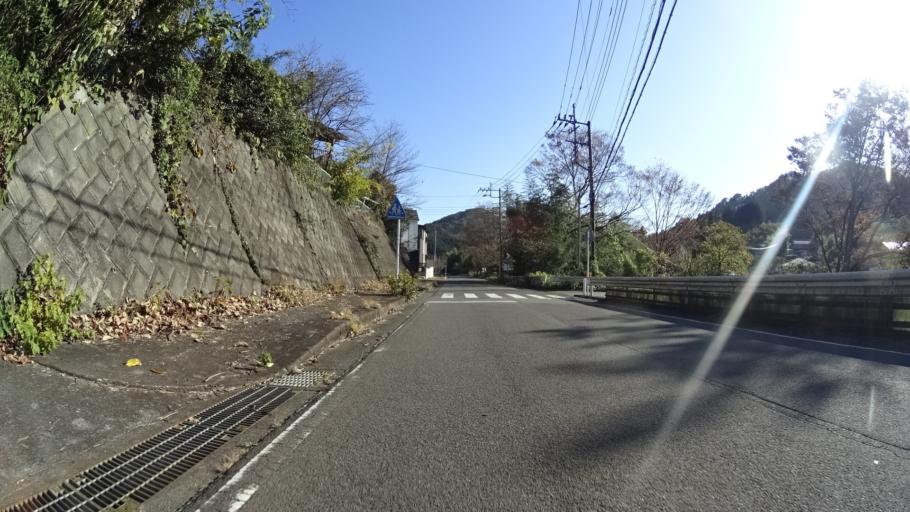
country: JP
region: Yamanashi
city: Uenohara
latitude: 35.6459
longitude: 139.1251
